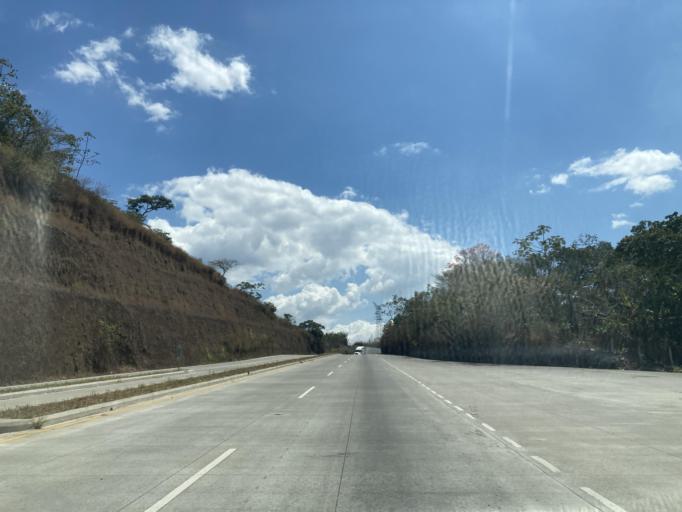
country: GT
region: Santa Rosa
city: Barberena
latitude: 14.2919
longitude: -90.3494
